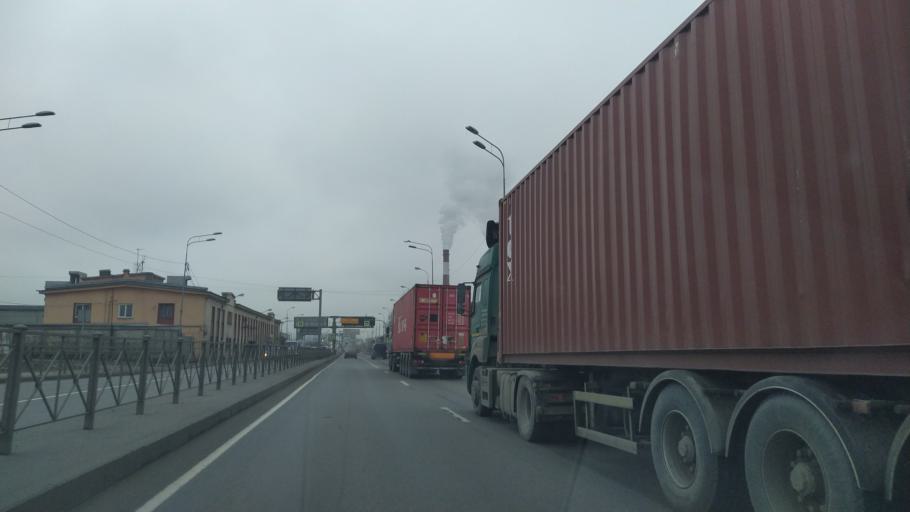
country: RU
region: St.-Petersburg
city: Dachnoye
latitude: 59.8324
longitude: 30.3065
